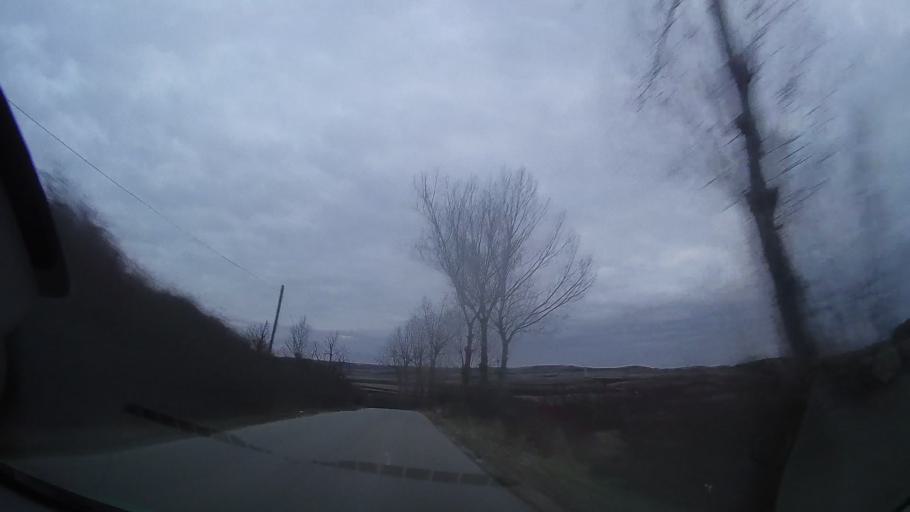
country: RO
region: Cluj
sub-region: Comuna Caianu
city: Caianu
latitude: 46.8043
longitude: 23.9301
